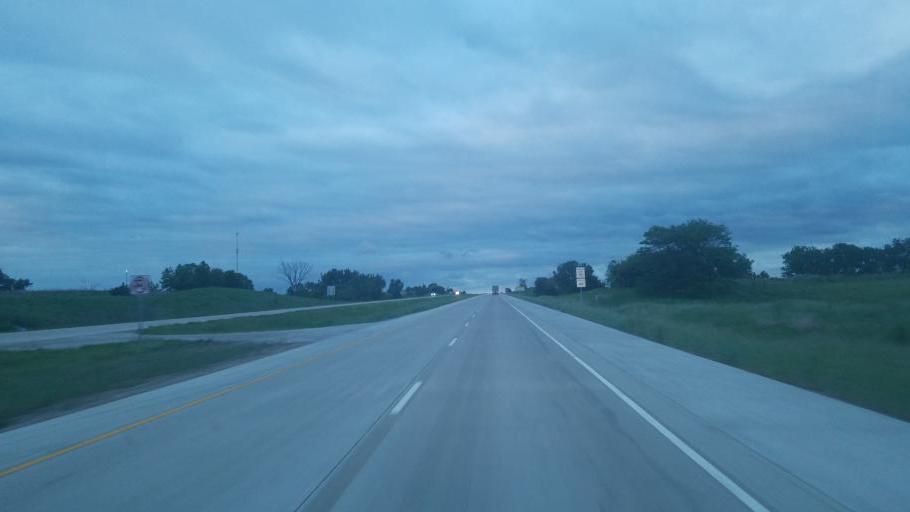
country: US
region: Iowa
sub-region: Decatur County
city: Lamoni
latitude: 40.5831
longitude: -93.9287
